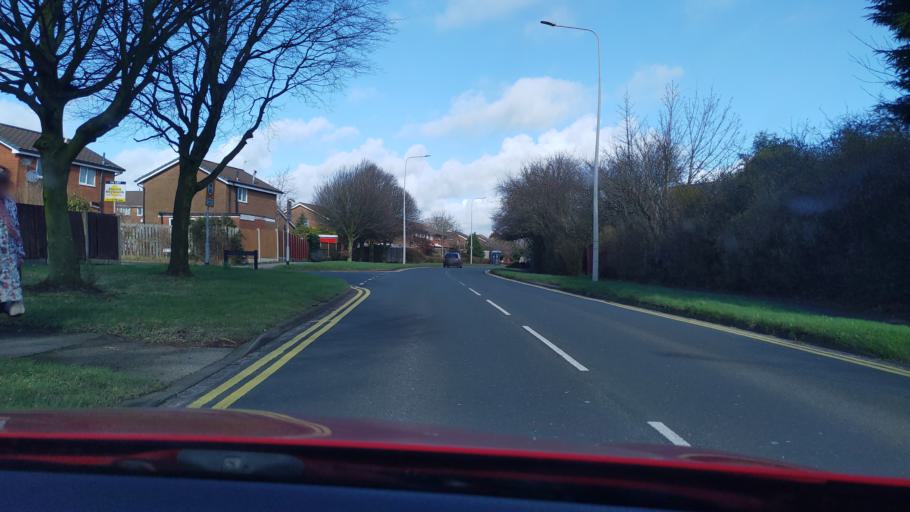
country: GB
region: England
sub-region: Lancashire
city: Preston
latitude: 53.7900
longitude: -2.6982
